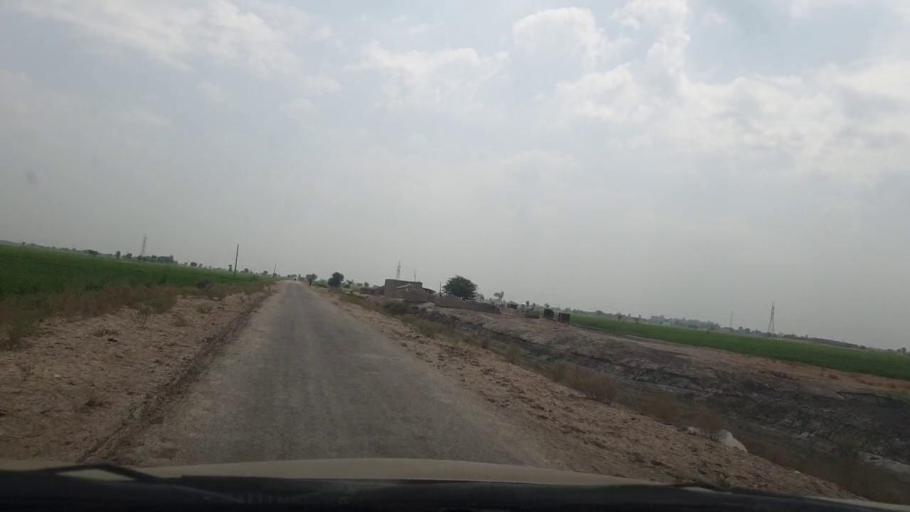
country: PK
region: Sindh
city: Ratodero
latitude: 27.7014
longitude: 68.2478
